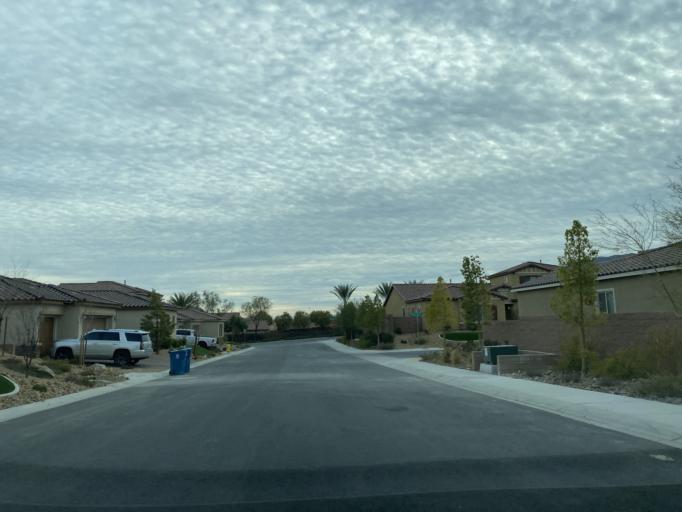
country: US
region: Nevada
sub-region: Clark County
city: Summerlin South
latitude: 36.2763
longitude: -115.3248
